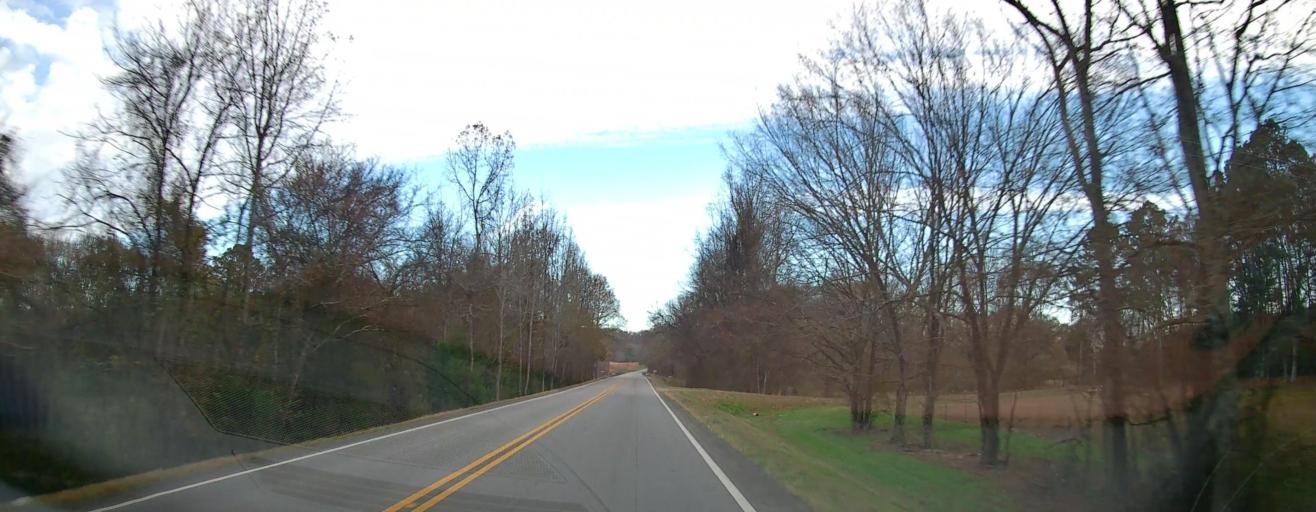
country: US
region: Alabama
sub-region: Marshall County
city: Arab
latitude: 34.3874
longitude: -86.6651
